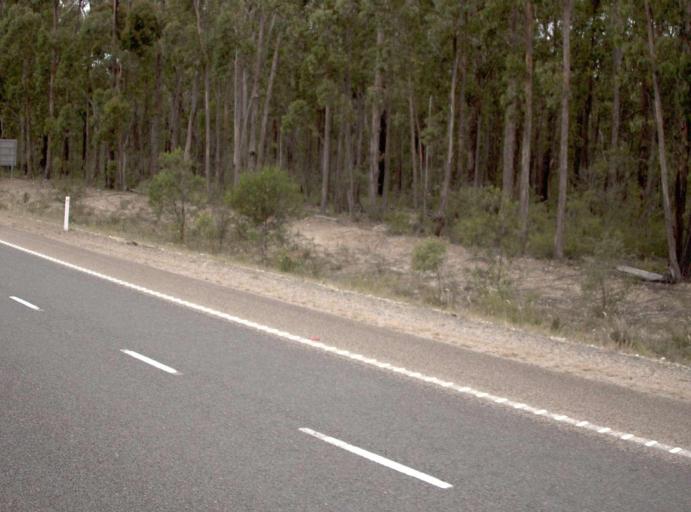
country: AU
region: Victoria
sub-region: East Gippsland
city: Lakes Entrance
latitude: -37.7015
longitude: 147.9934
